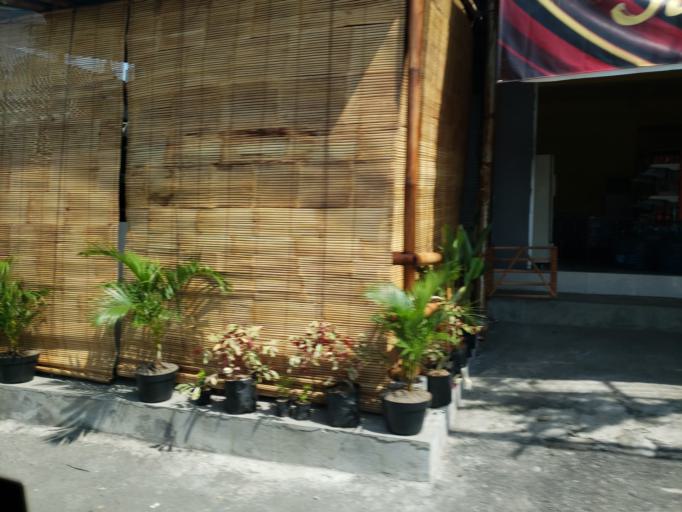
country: ID
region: Bali
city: Kangin
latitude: -8.8228
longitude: 115.1432
